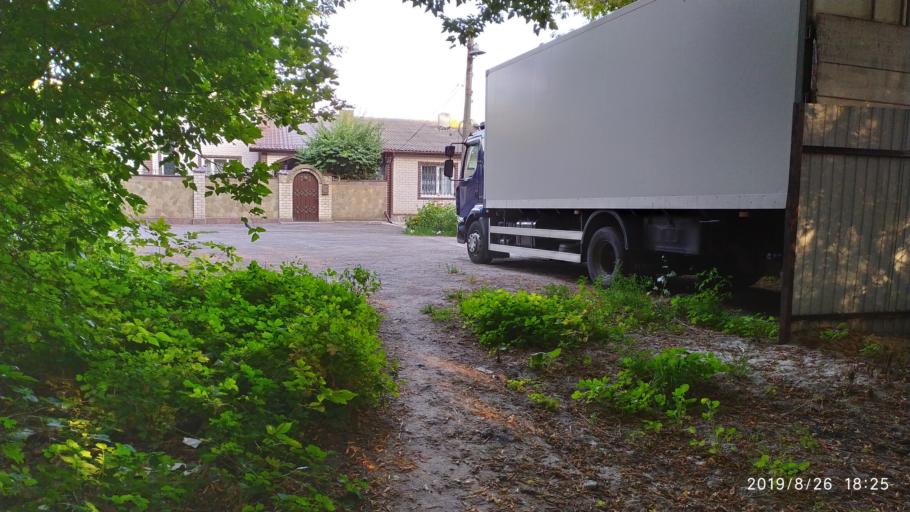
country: RU
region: Kursk
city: Kursk
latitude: 51.6489
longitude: 36.1346
